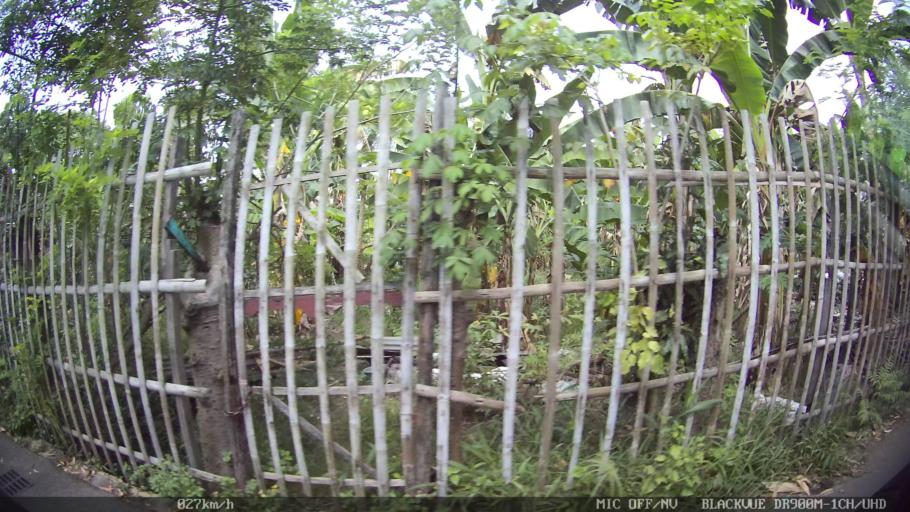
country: ID
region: Daerah Istimewa Yogyakarta
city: Yogyakarta
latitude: -7.7948
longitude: 110.3892
